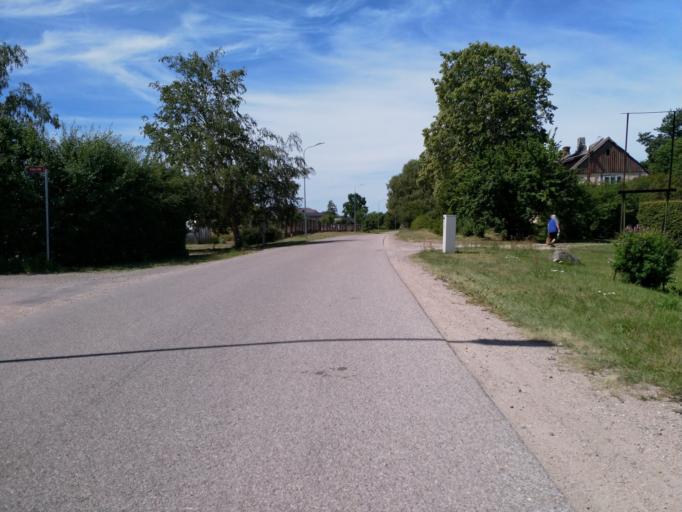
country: LV
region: Grobina
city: Grobina
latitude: 56.5371
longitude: 21.1543
